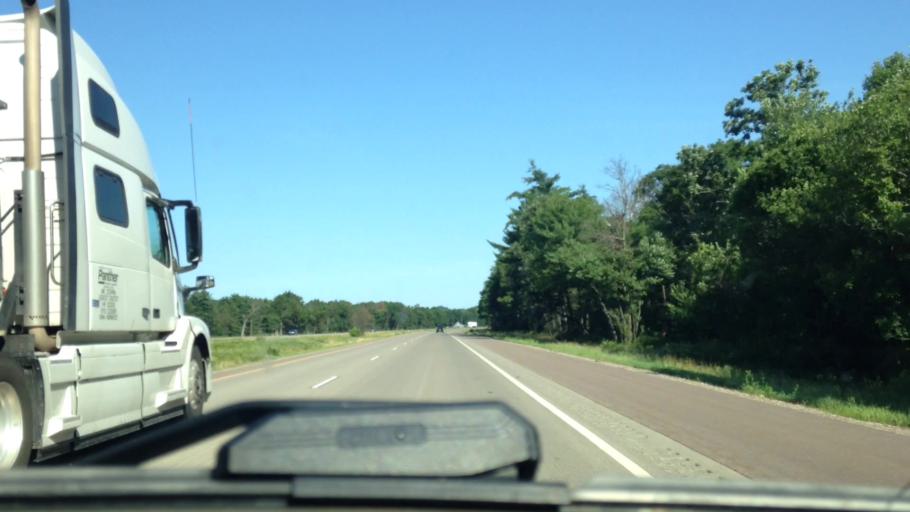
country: US
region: Wisconsin
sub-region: Jackson County
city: Black River Falls
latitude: 44.3529
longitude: -90.9458
